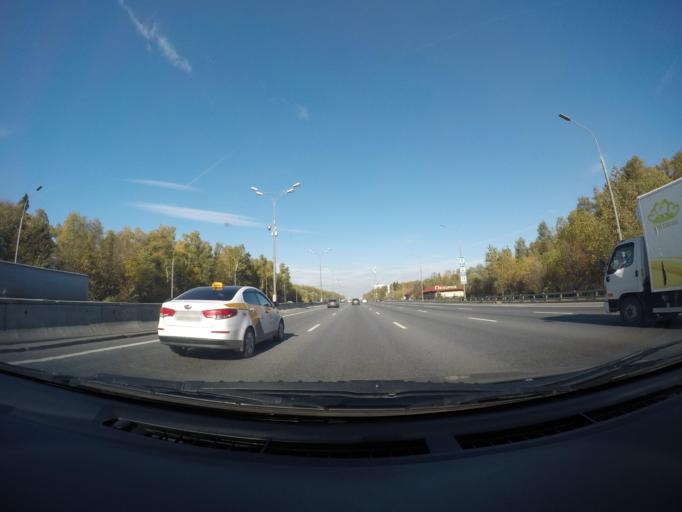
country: RU
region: Moscow
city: Ivanovskoye
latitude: 55.7919
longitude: 37.8412
